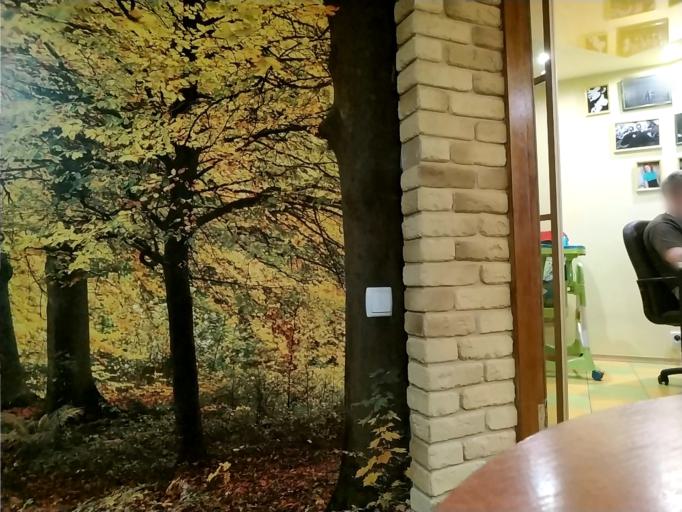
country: RU
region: Tverskaya
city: Zapadnaya Dvina
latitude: 56.3299
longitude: 31.8918
